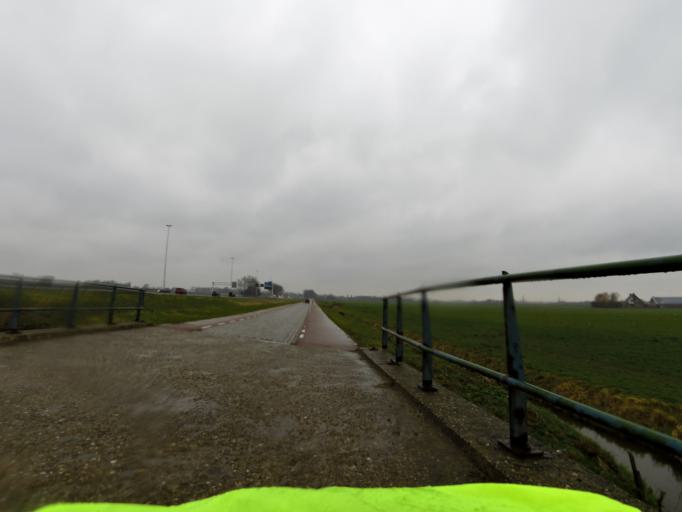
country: NL
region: South Holland
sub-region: Gemeente Maassluis
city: Maassluis
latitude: 51.9220
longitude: 4.2917
